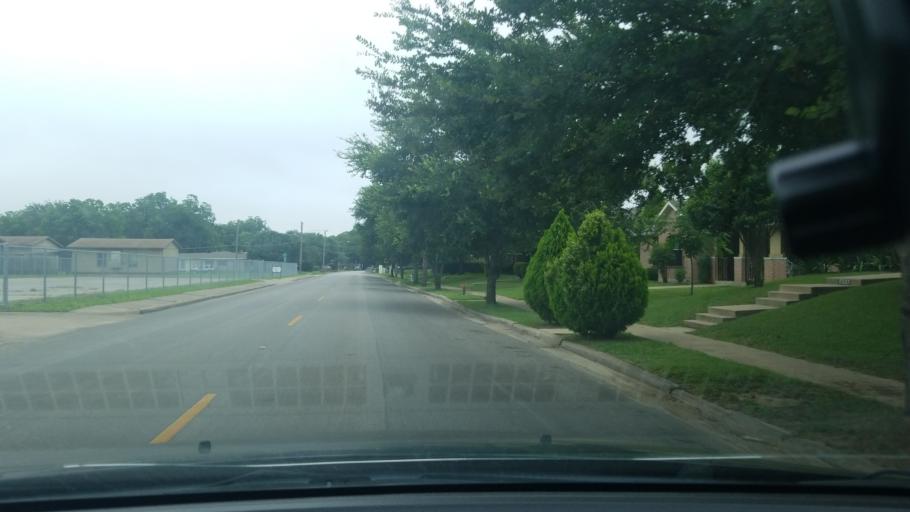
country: US
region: Texas
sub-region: Dallas County
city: Balch Springs
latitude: 32.7571
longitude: -96.6868
